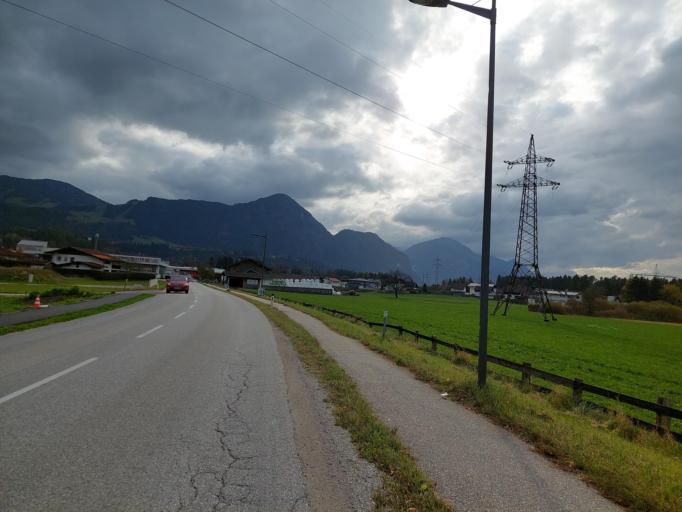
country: AT
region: Tyrol
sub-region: Politischer Bezirk Kufstein
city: Kramsach
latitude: 47.4404
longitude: 11.8739
